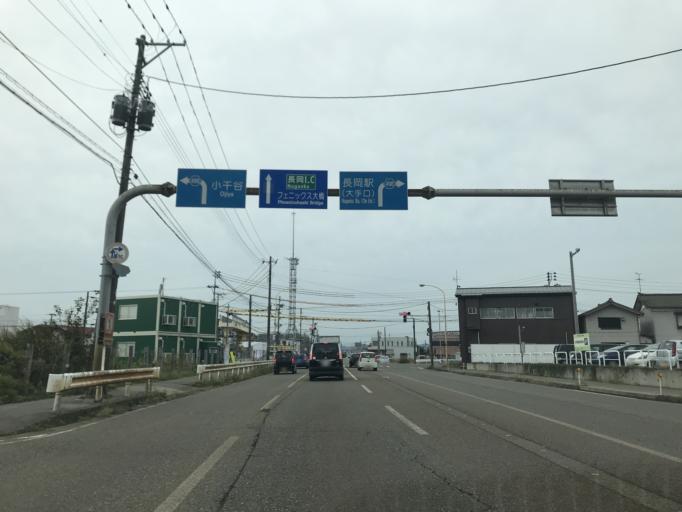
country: JP
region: Niigata
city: Nagaoka
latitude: 37.4261
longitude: 138.8399
